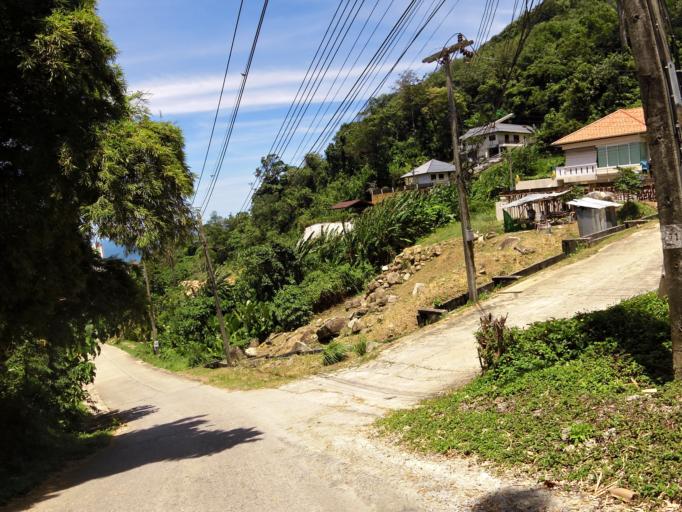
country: TH
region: Phuket
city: Ban Karon
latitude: 7.8505
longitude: 98.3058
